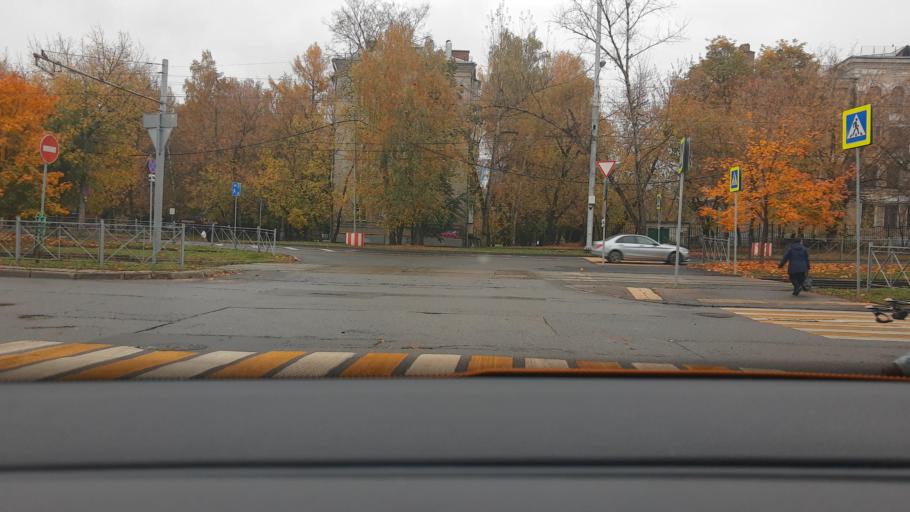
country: RU
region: Moscow
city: Metrogorodok
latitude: 55.8260
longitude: 37.7605
